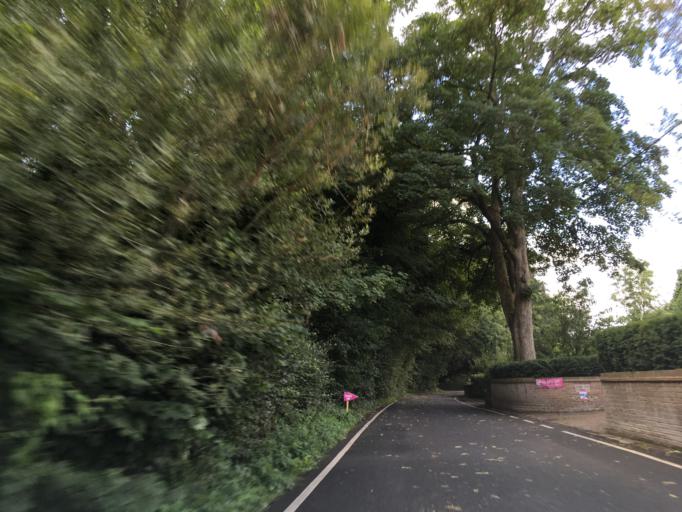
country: GB
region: England
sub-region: Hampshire
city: Overton
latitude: 51.2020
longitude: -1.3694
